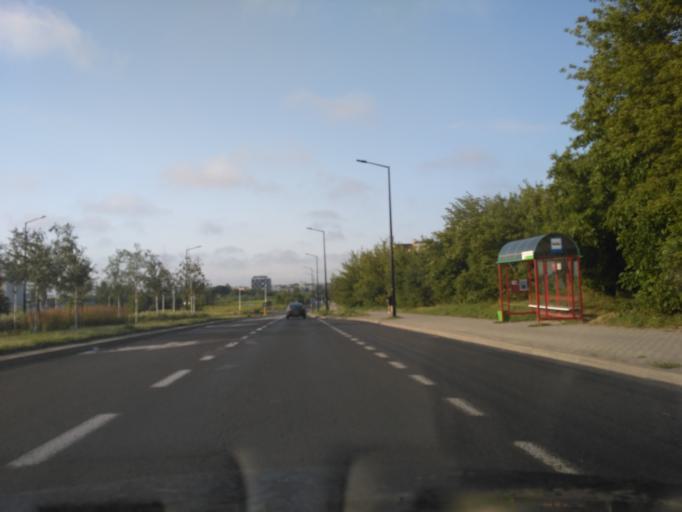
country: PL
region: Lublin Voivodeship
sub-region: Powiat lubelski
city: Lublin
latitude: 51.2626
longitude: 22.5581
